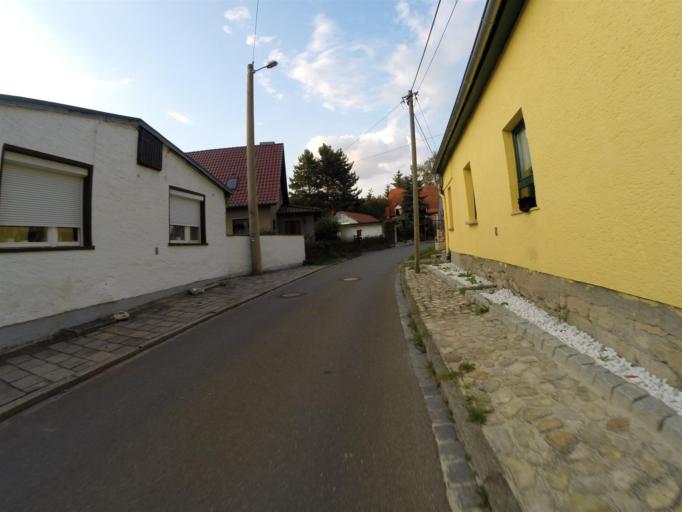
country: DE
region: Thuringia
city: Grosslobichau
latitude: 50.9294
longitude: 11.6530
